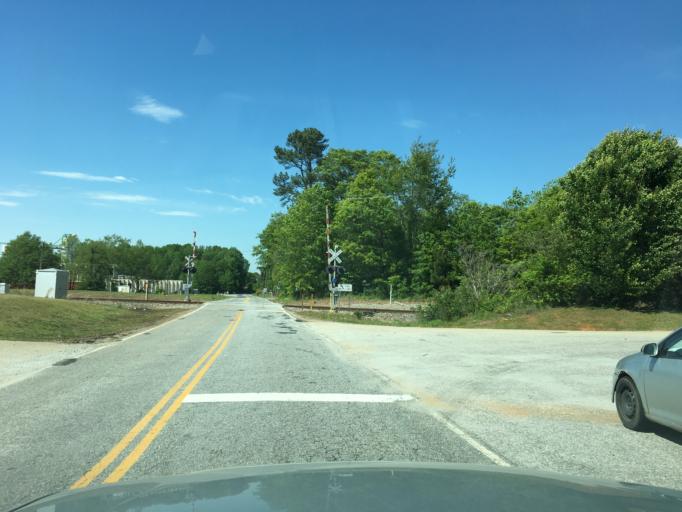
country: US
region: South Carolina
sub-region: Spartanburg County
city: Southern Shops
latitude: 34.9926
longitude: -82.0185
